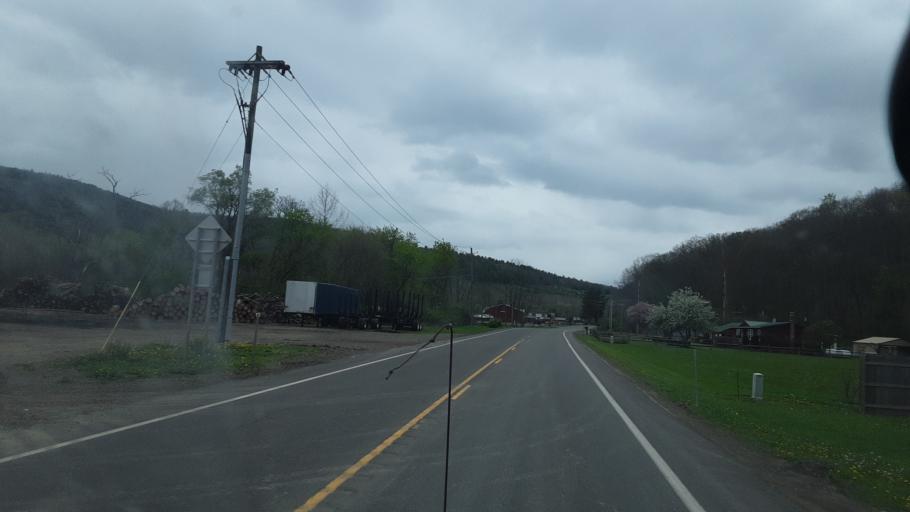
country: US
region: New York
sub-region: Steuben County
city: Addison
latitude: 42.0876
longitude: -77.2464
